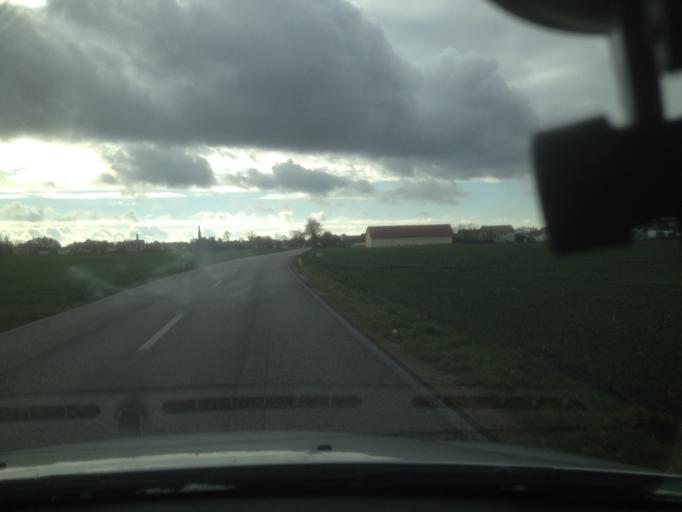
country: DE
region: Bavaria
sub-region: Upper Bavaria
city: Prittriching
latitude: 48.2150
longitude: 10.9340
